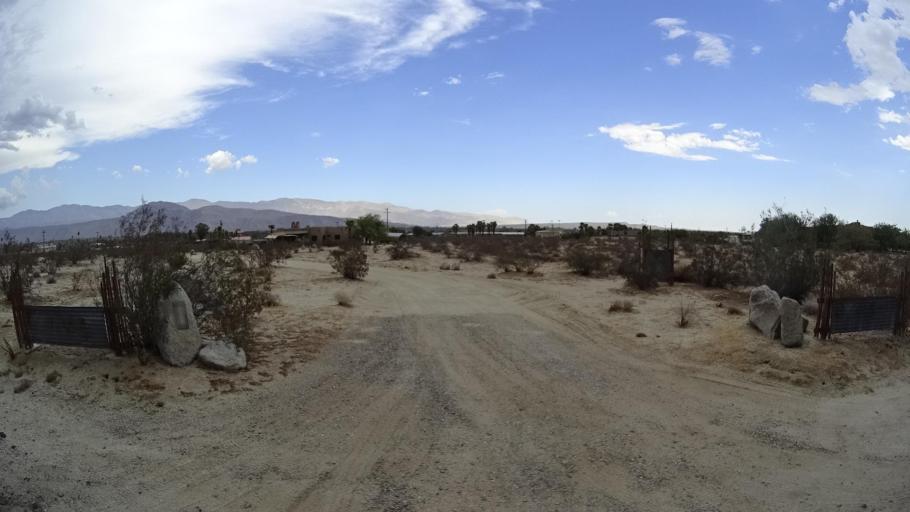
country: US
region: California
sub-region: San Diego County
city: Borrego Springs
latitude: 33.2635
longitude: -116.3877
